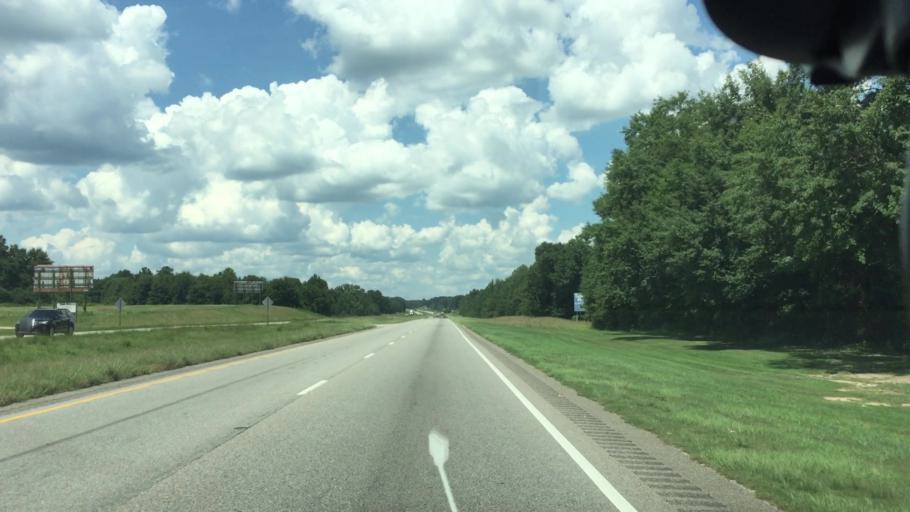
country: US
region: Alabama
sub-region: Pike County
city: Troy
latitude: 31.8564
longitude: -85.9971
